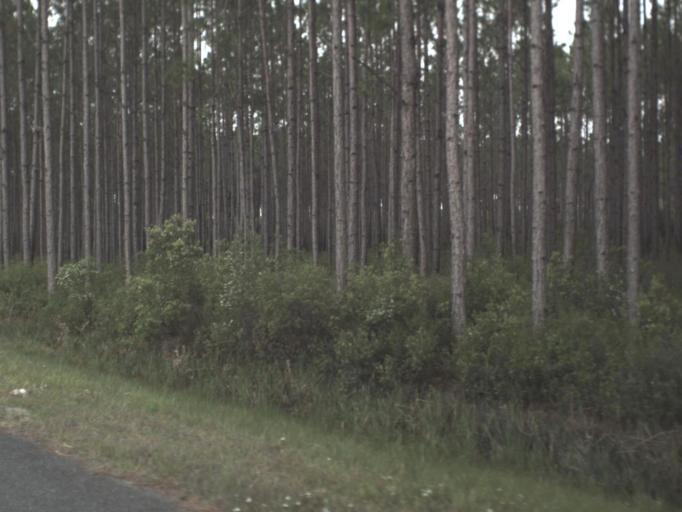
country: US
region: Florida
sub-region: Franklin County
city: Eastpoint
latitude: 29.8027
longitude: -84.8340
